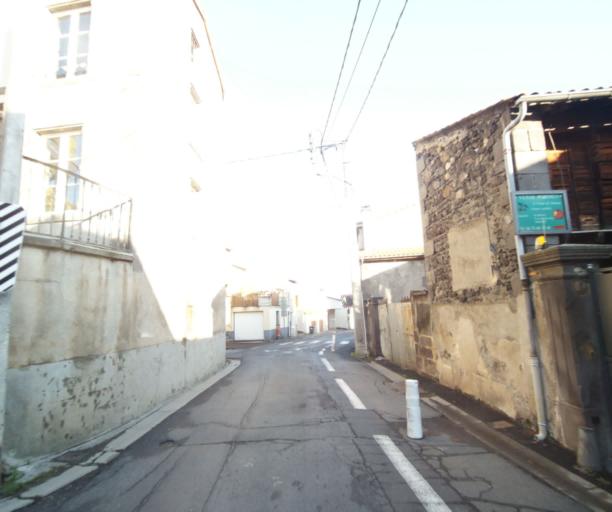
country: FR
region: Auvergne
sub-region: Departement du Puy-de-Dome
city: Nohanent
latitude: 45.8105
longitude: 3.0567
